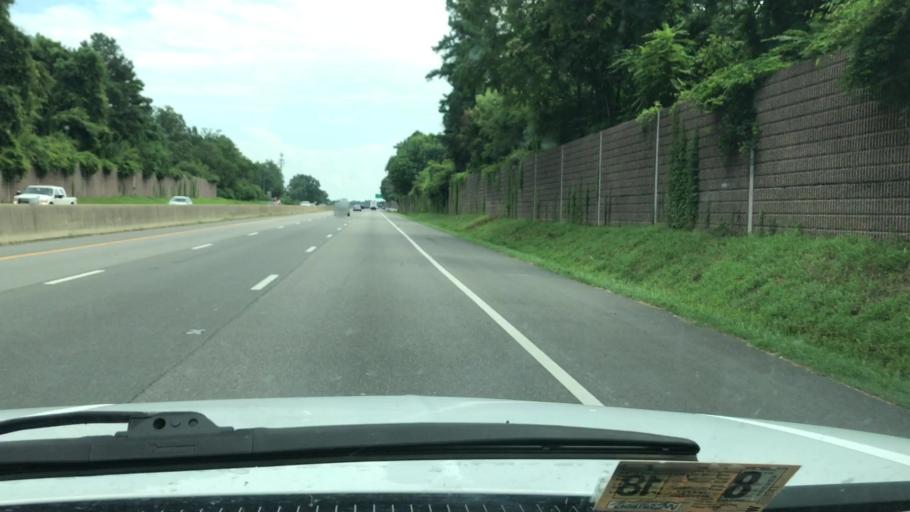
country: US
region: Virginia
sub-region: Chesterfield County
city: Bon Air
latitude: 37.4866
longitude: -77.5188
